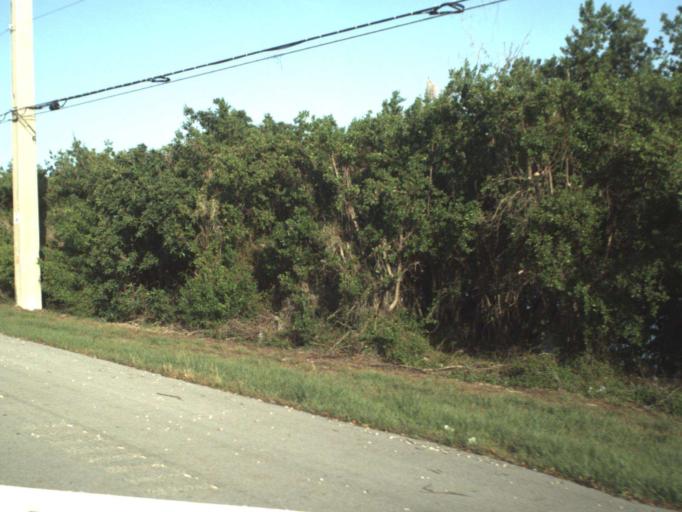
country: US
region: Florida
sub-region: Monroe County
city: Marathon
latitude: 24.7860
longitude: -80.8983
